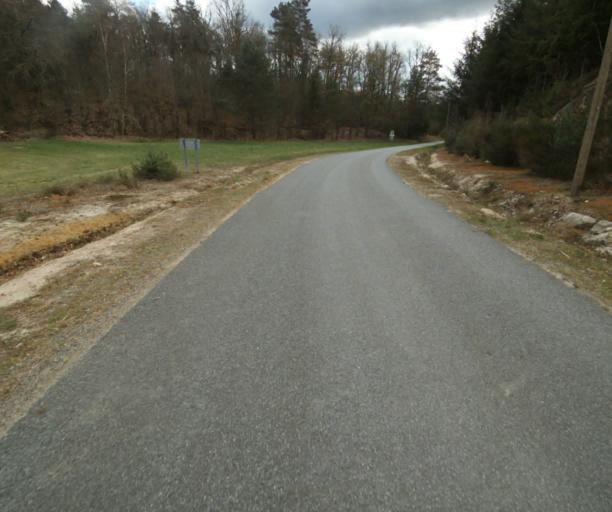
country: FR
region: Limousin
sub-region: Departement de la Correze
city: Correze
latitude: 45.3104
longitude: 1.9333
